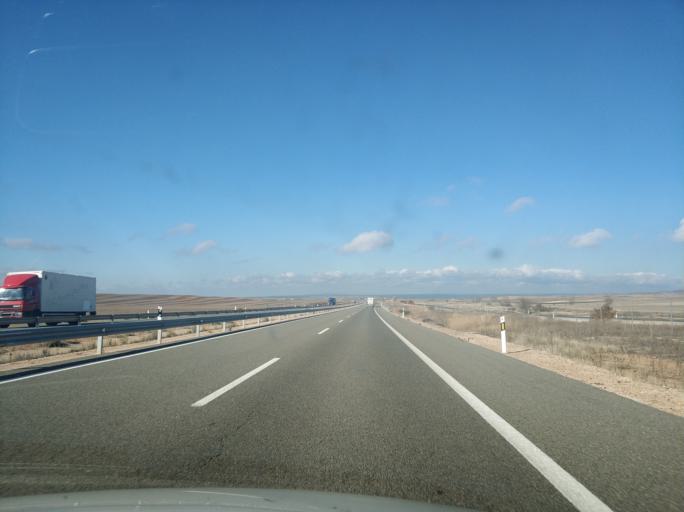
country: ES
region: Castille and Leon
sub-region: Provincia de Soria
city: Coscurita
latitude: 41.3986
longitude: -2.4760
